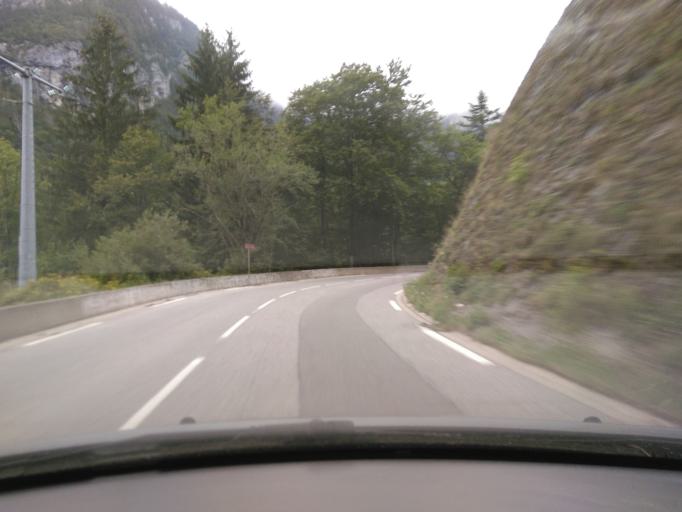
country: FR
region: Rhone-Alpes
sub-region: Departement de la Haute-Savoie
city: Le Grand-Bornand
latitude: 45.9912
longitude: 6.3949
